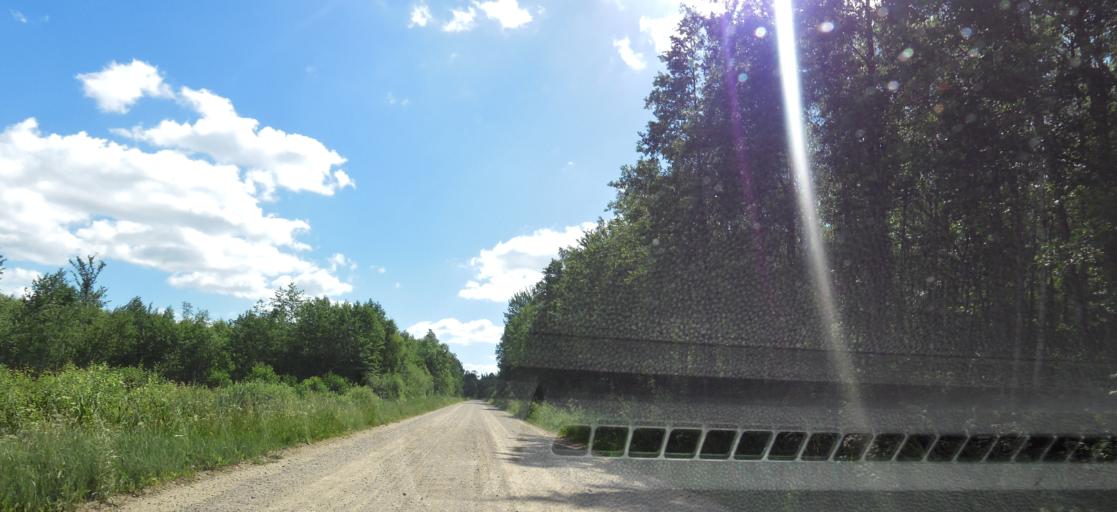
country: LT
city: Vabalninkas
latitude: 56.0013
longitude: 24.8786
